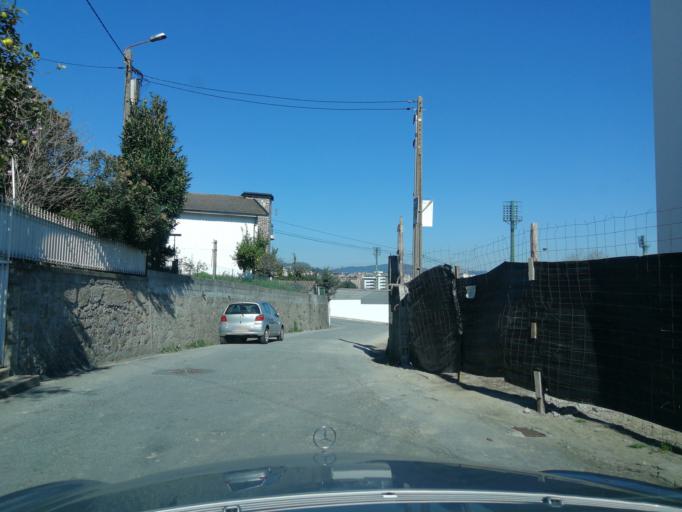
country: PT
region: Braga
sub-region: Vila Nova de Famalicao
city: Calendario
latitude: 41.3996
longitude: -8.5243
